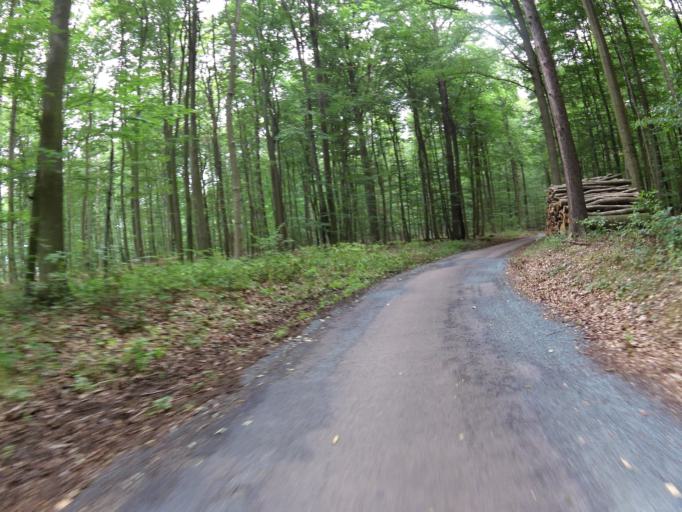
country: DE
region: Mecklenburg-Vorpommern
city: Seebad Heringsdorf
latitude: 53.8962
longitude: 14.1636
